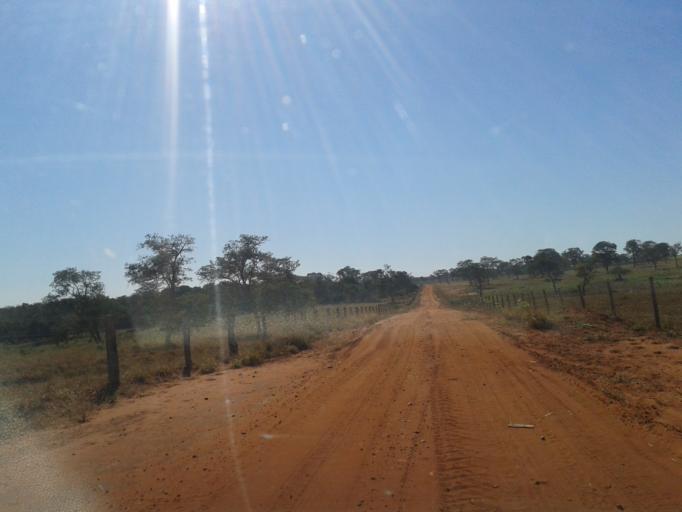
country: BR
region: Minas Gerais
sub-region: Santa Vitoria
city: Santa Vitoria
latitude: -19.0366
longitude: -50.3642
